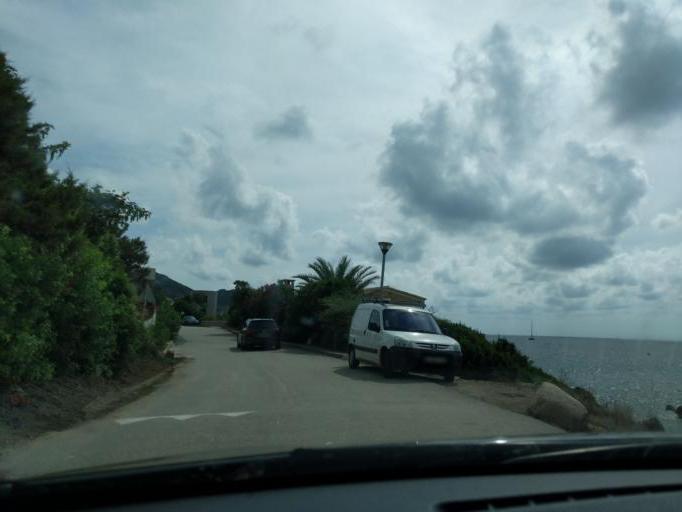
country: FR
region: Corsica
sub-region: Departement de la Corse-du-Sud
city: Propriano
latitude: 41.5420
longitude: 8.8516
